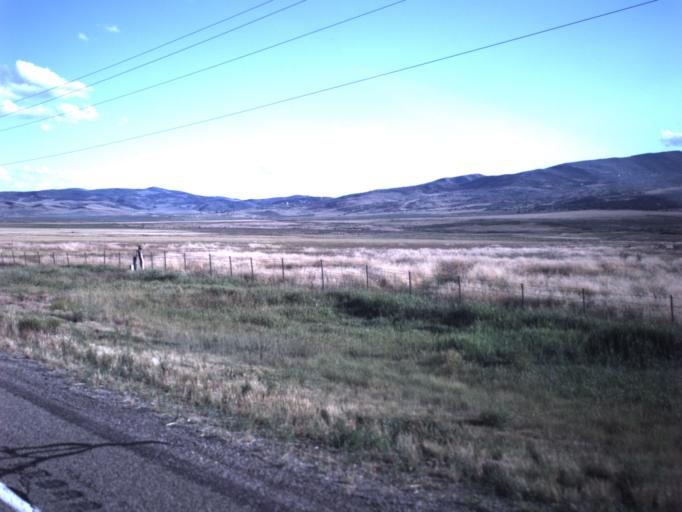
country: US
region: Utah
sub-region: Sanpete County
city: Fairview
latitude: 39.8011
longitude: -111.5015
